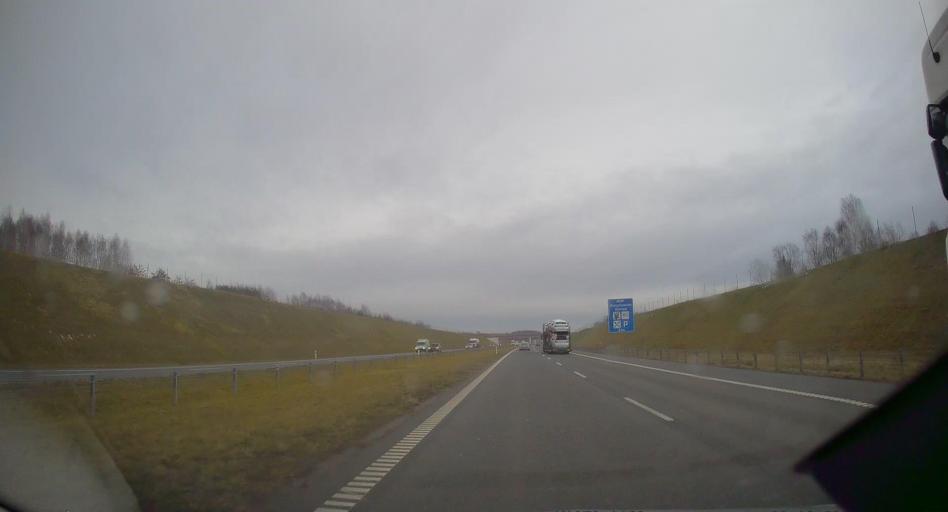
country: PL
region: Silesian Voivodeship
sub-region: Czestochowa
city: Czestochowa
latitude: 50.8732
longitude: 19.1044
